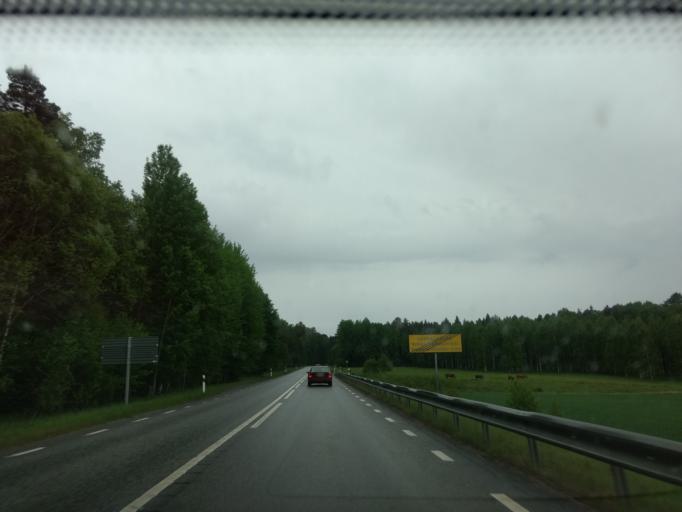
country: SE
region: Uppsala
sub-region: Uppsala Kommun
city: Saevja
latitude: 59.7809
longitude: 17.6639
